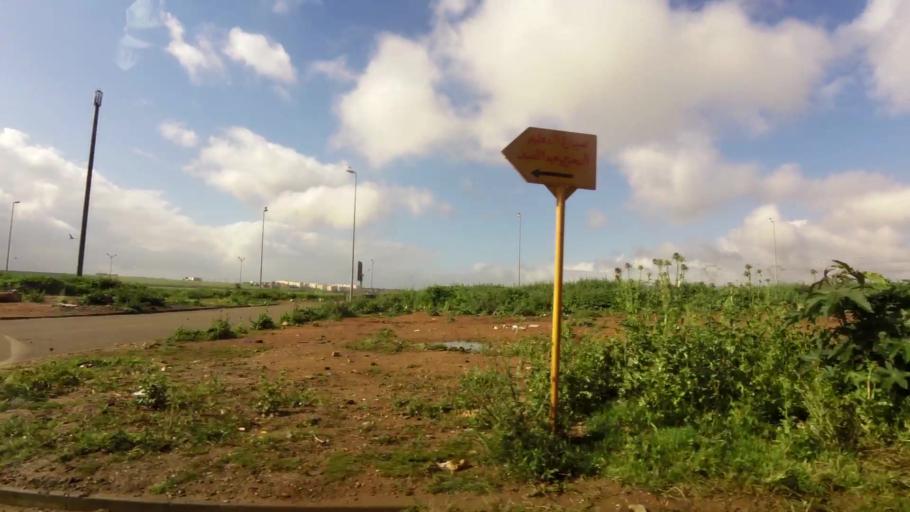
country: MA
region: Grand Casablanca
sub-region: Nouaceur
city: Bouskoura
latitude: 33.5337
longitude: -7.7050
